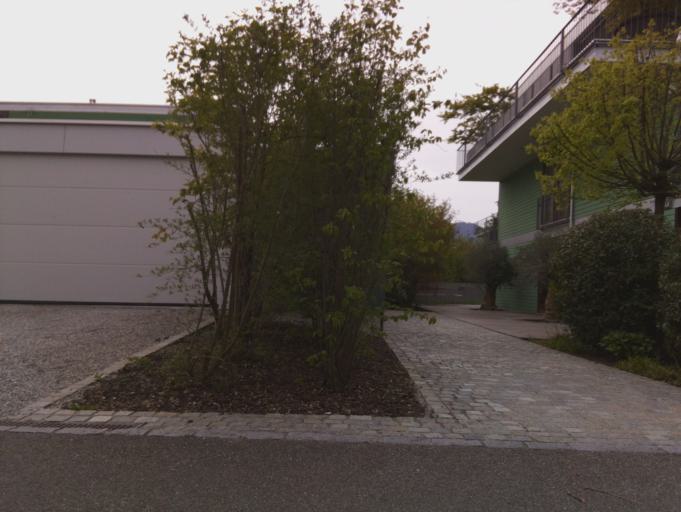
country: CH
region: Schwyz
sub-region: Bezirk March
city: Lachen
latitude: 47.1909
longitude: 8.8435
